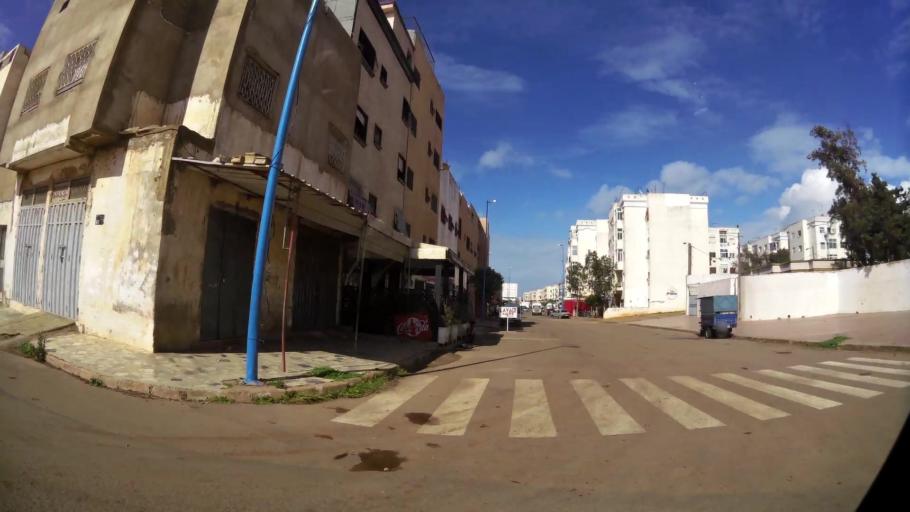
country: MA
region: Grand Casablanca
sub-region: Casablanca
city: Casablanca
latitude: 33.5641
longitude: -7.6963
